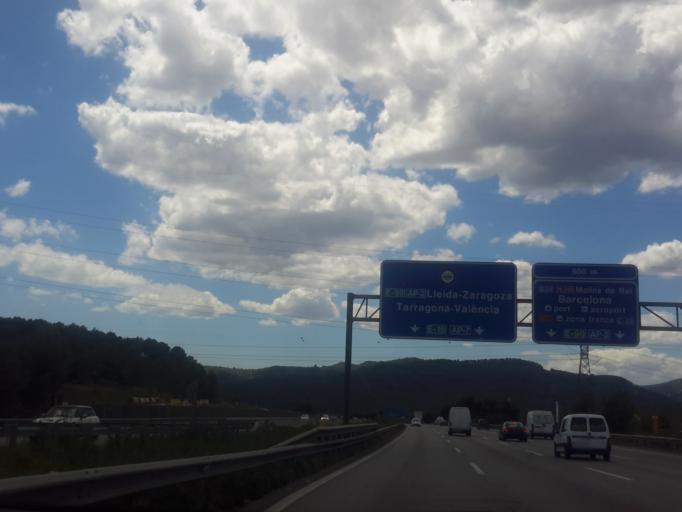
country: ES
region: Catalonia
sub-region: Provincia de Barcelona
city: Castellbisbal
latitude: 41.4567
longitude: 2.0049
